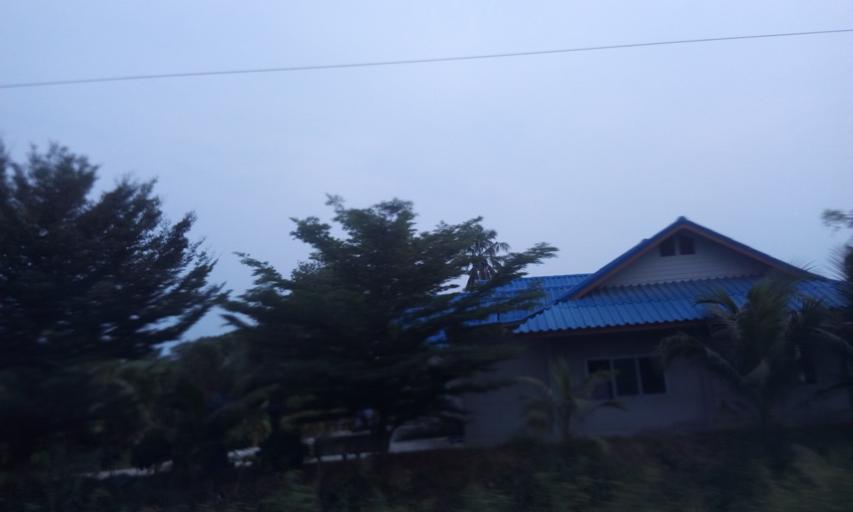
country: TH
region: Chachoengsao
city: Ban Pho
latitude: 13.6017
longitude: 101.1537
